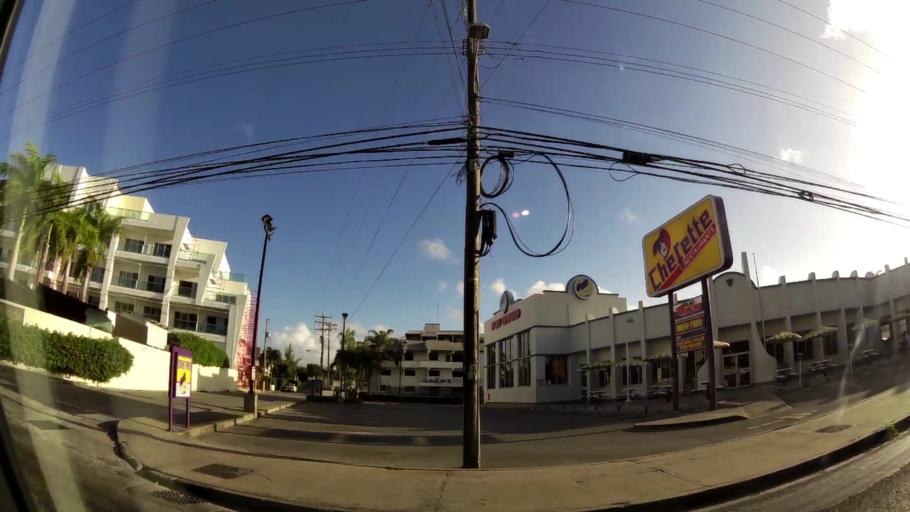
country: BB
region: Saint Michael
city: Bridgetown
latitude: 13.0743
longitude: -59.5888
